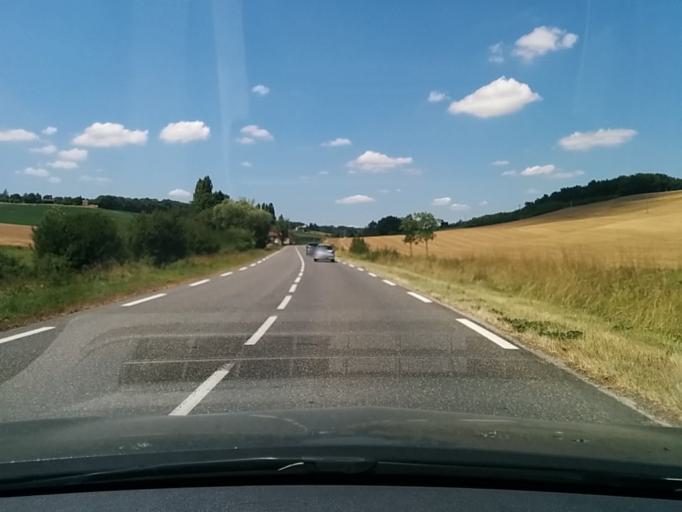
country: FR
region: Midi-Pyrenees
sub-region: Departement du Gers
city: Vic-Fezensac
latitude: 43.7371
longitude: 0.3596
